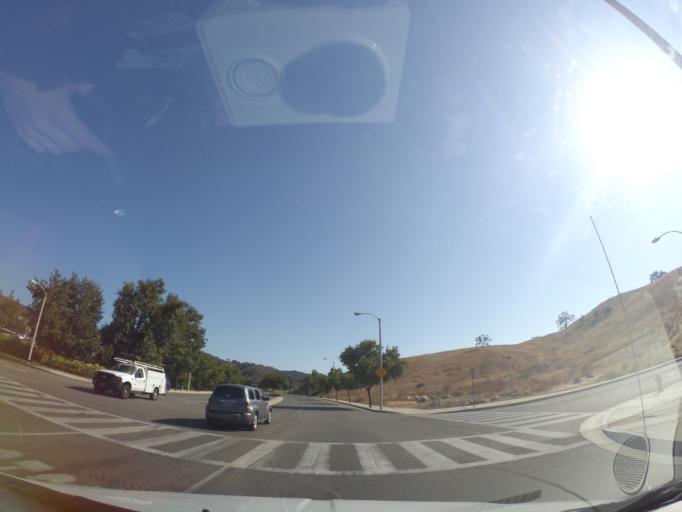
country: US
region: California
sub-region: Los Angeles County
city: Agoura
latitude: 34.1292
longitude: -118.7083
